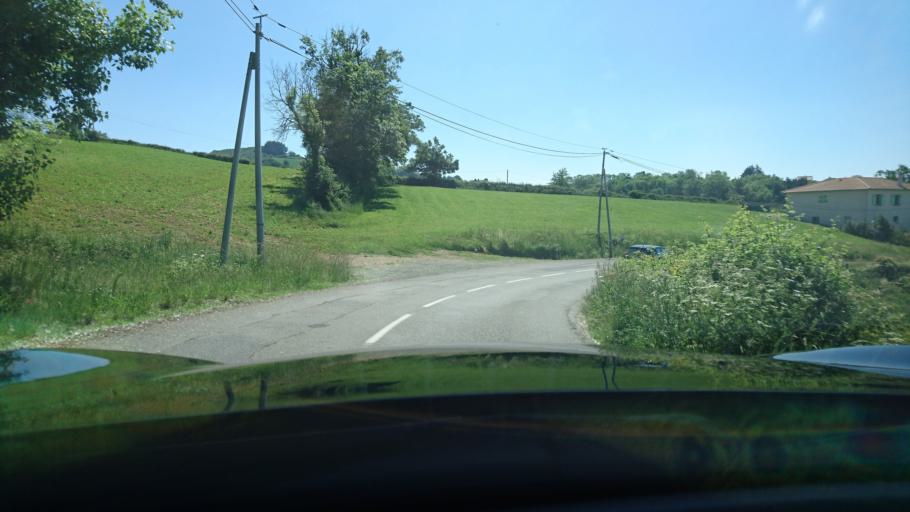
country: FR
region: Rhone-Alpes
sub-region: Departement de la Loire
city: Bussieres
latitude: 45.8433
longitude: 4.2676
